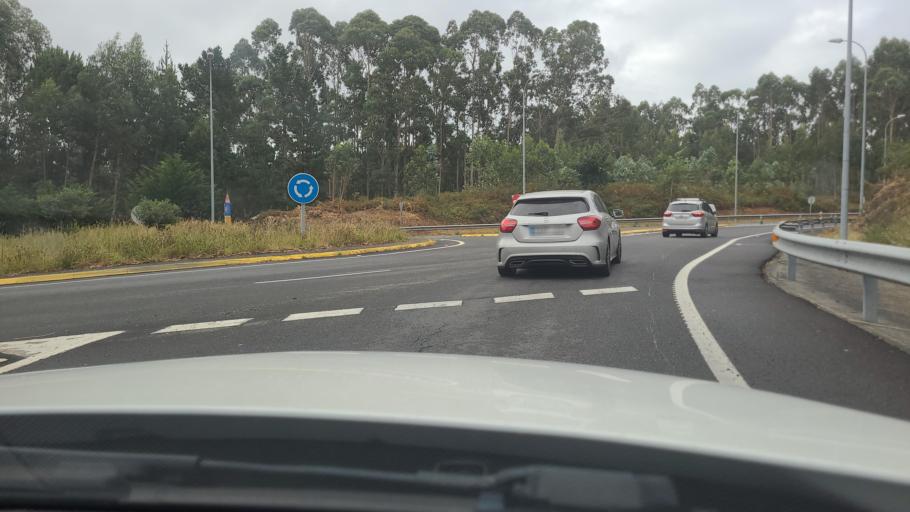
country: ES
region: Galicia
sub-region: Provincia da Coruna
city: Corcubion
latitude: 42.9441
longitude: -9.2246
